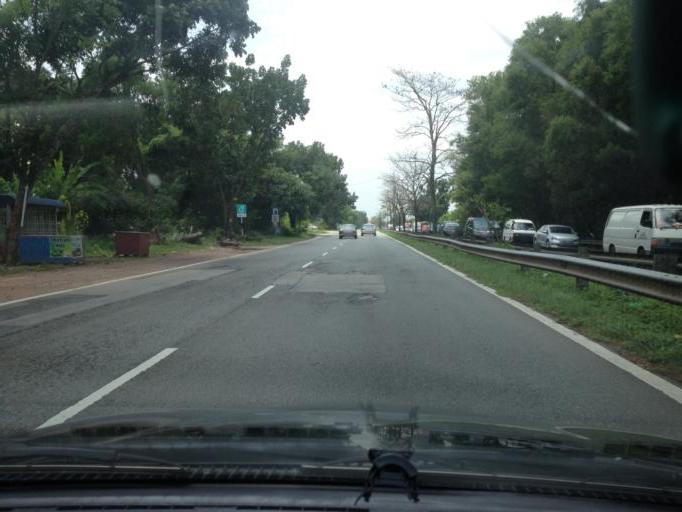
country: MY
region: Kedah
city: Sungai Petani
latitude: 5.6388
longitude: 100.5394
